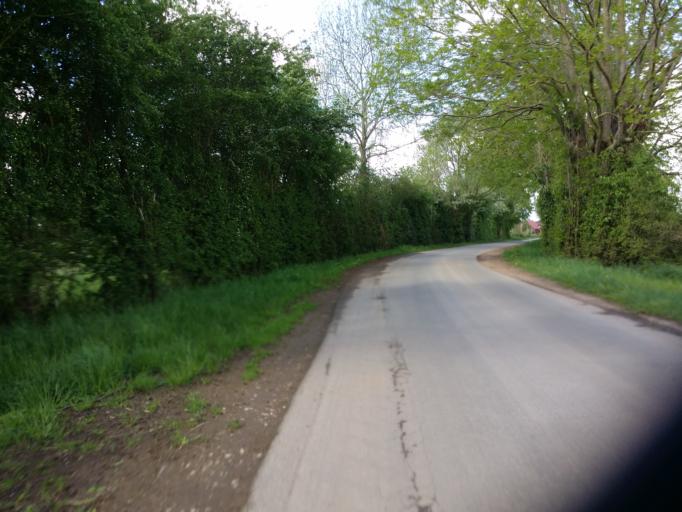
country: DE
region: Lower Saxony
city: Ahsen-Oetzen
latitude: 52.9778
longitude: 9.1214
